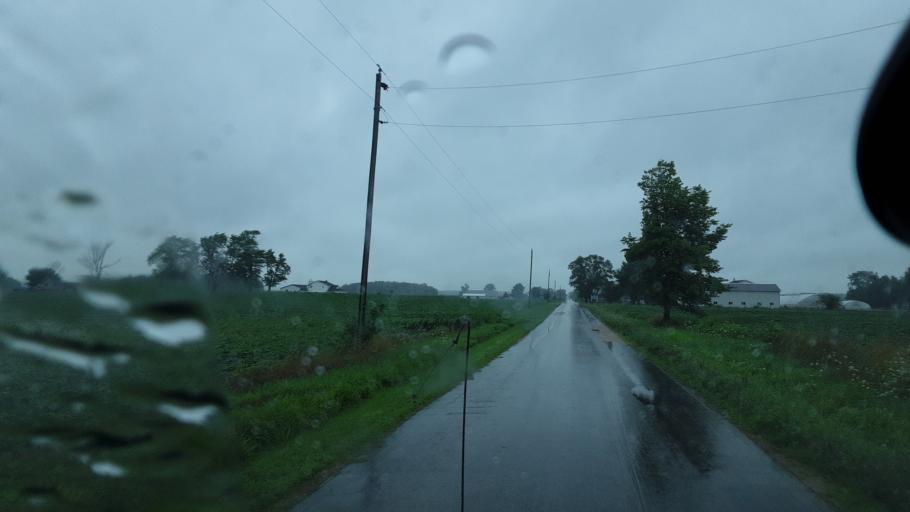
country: US
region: Indiana
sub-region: Adams County
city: Berne
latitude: 40.6922
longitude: -84.8118
